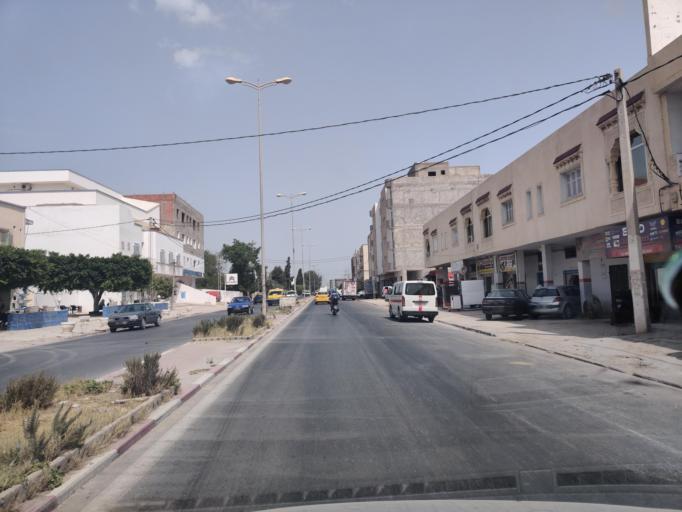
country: TN
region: Nabul
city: Bu `Urqub
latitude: 36.5864
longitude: 10.5070
